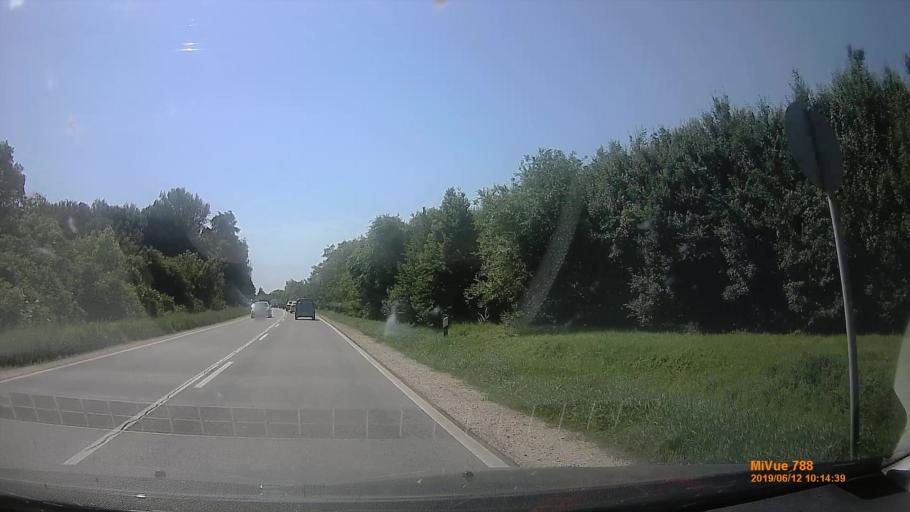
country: HU
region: Pest
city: Dabas
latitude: 47.2103
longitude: 19.2848
